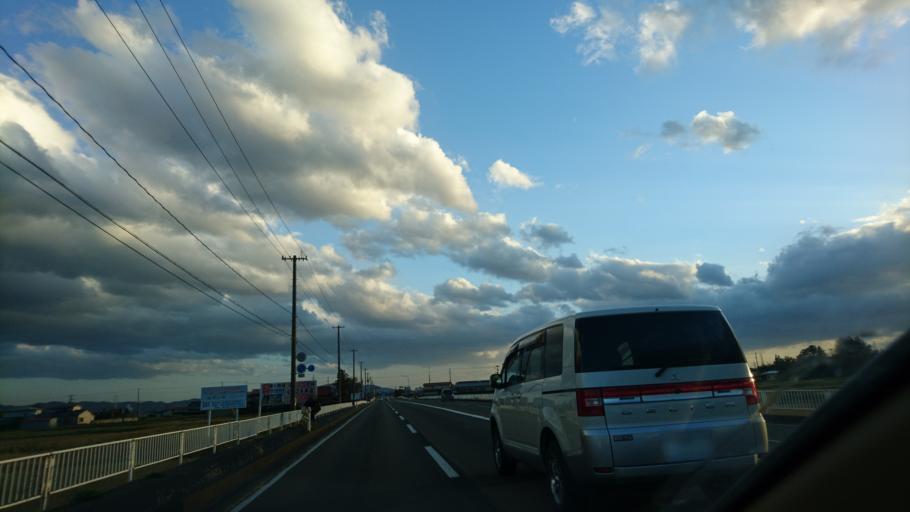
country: JP
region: Iwate
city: Mizusawa
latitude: 39.1623
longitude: 141.1329
